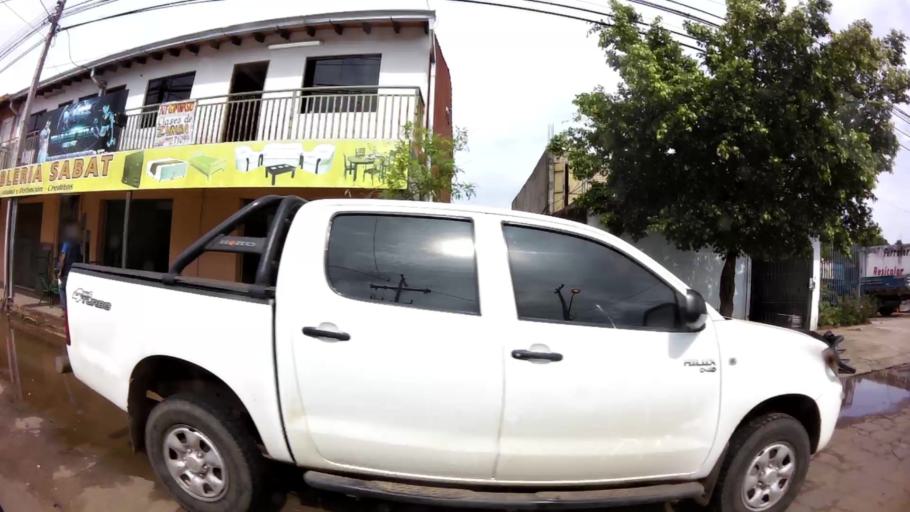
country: PY
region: Central
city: Limpio
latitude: -25.1723
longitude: -57.4729
